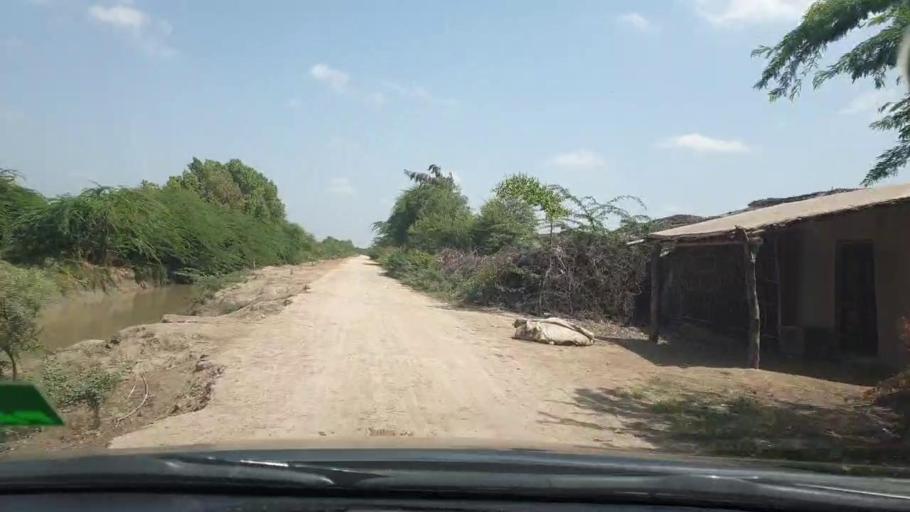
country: PK
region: Sindh
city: Tando Bago
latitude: 24.8796
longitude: 69.1009
